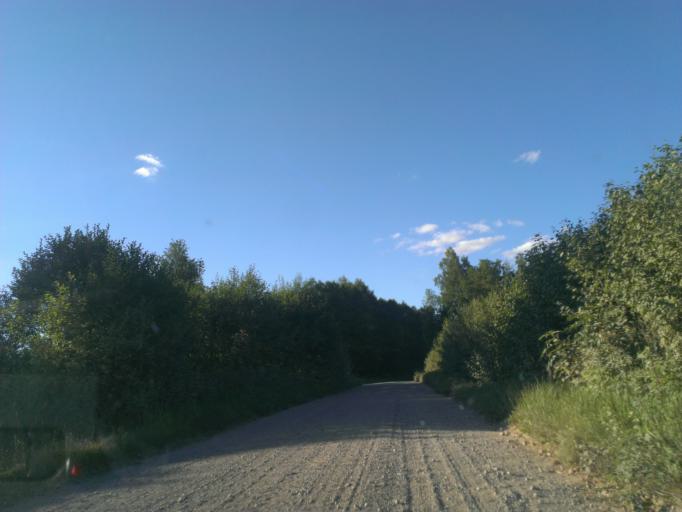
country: LV
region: Malpils
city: Malpils
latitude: 57.0877
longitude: 25.0499
